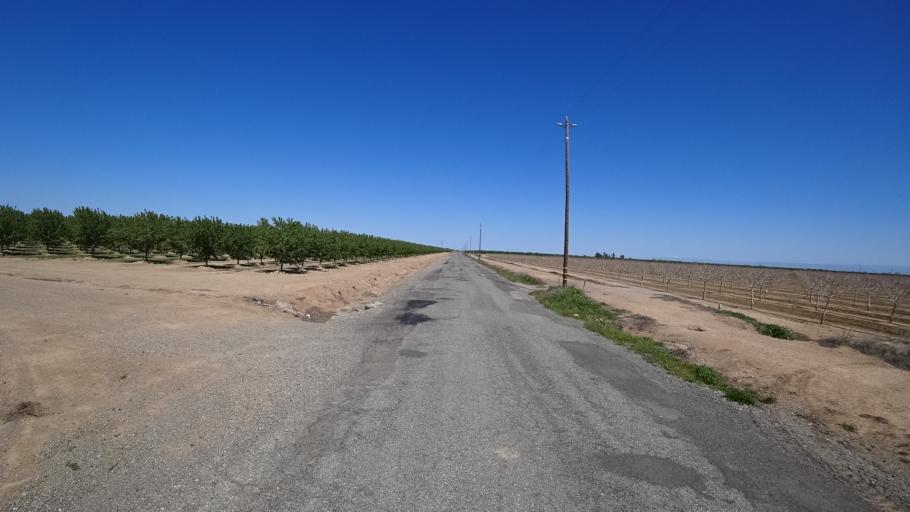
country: US
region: California
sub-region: Glenn County
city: Orland
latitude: 39.6354
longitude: -122.2347
